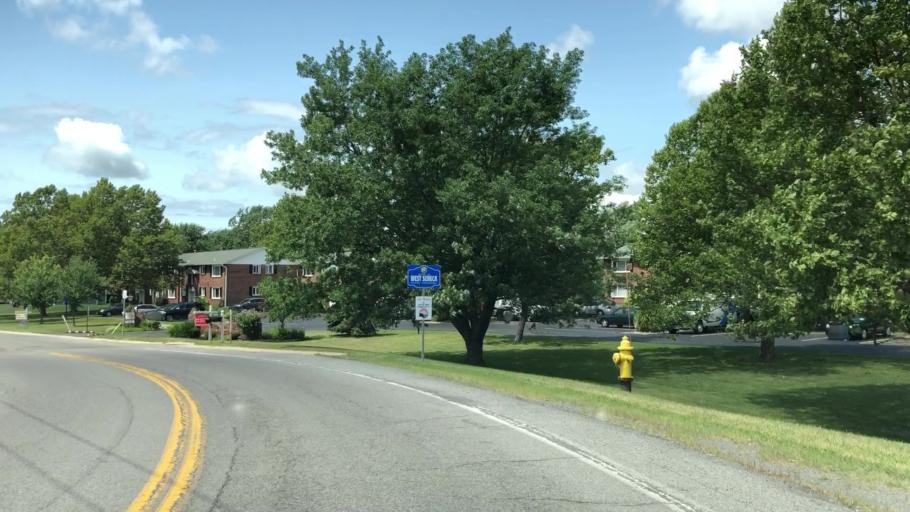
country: US
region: New York
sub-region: Erie County
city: Orchard Park
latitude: 42.8112
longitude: -78.7257
